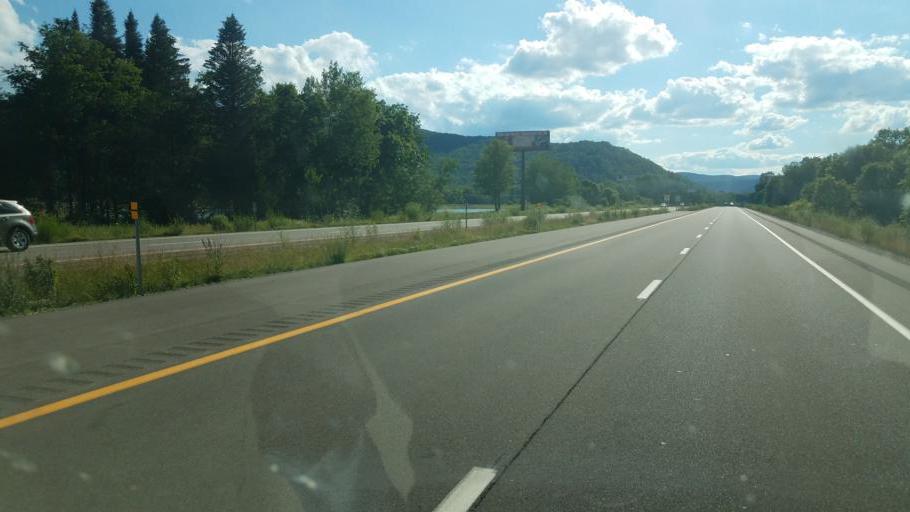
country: US
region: New York
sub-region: Cattaraugus County
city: Allegany
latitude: 42.0861
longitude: -78.5962
